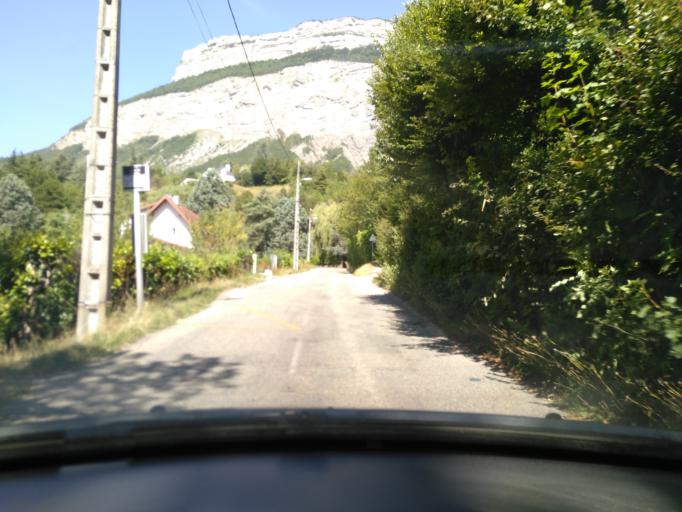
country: FR
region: Rhone-Alpes
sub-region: Departement de l'Isere
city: Meylan
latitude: 45.2260
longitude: 5.7843
